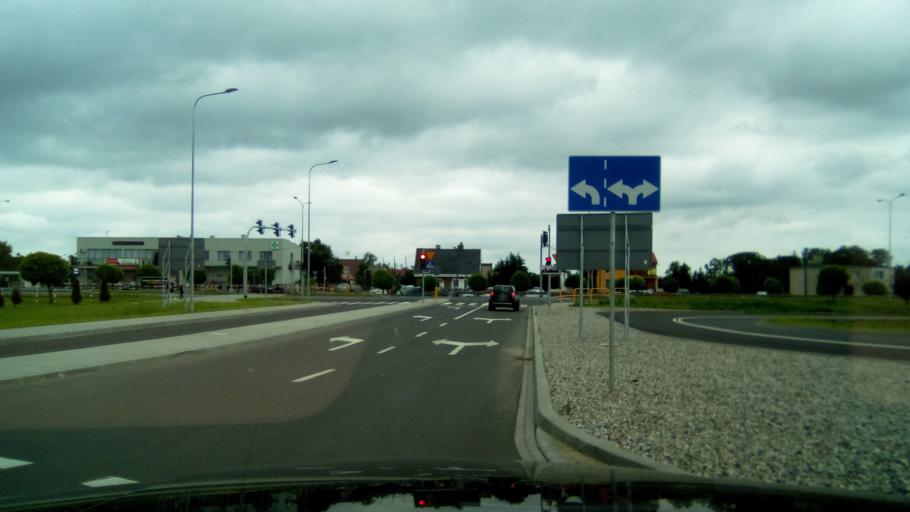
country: PL
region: Greater Poland Voivodeship
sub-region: Powiat gnieznienski
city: Gniezno
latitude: 52.5337
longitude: 17.5572
